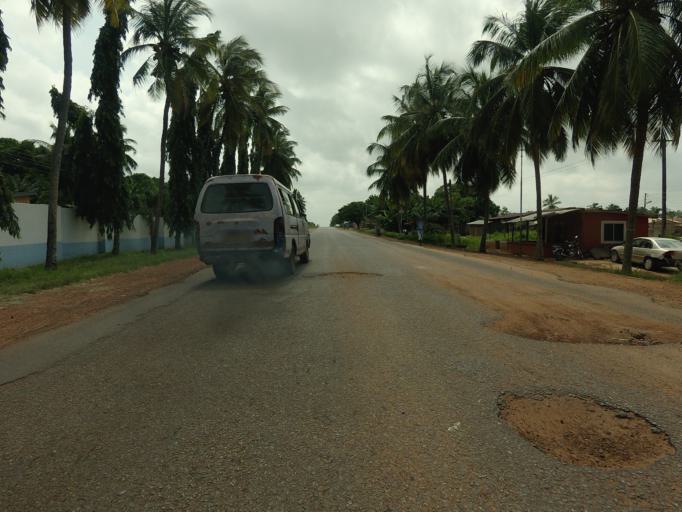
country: TG
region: Maritime
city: Lome
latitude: 6.1236
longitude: 1.1276
